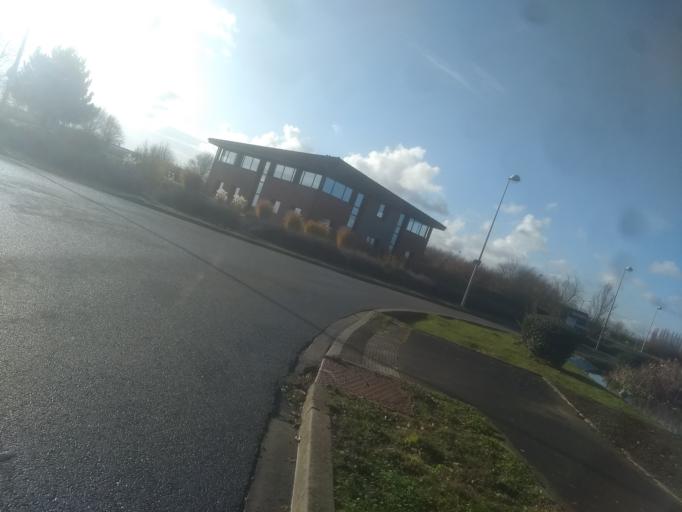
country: FR
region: Nord-Pas-de-Calais
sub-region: Departement du Pas-de-Calais
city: Anzin-Saint-Aubin
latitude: 50.3052
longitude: 2.7296
